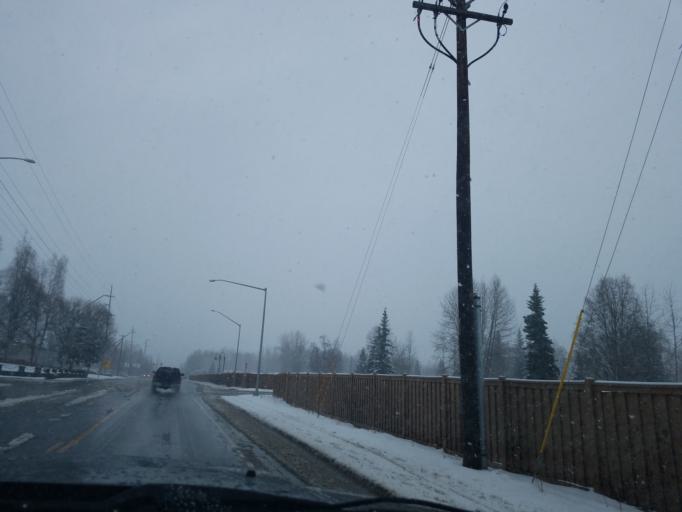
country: US
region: Alaska
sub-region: Anchorage Municipality
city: Anchorage
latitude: 61.1837
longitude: -149.8980
